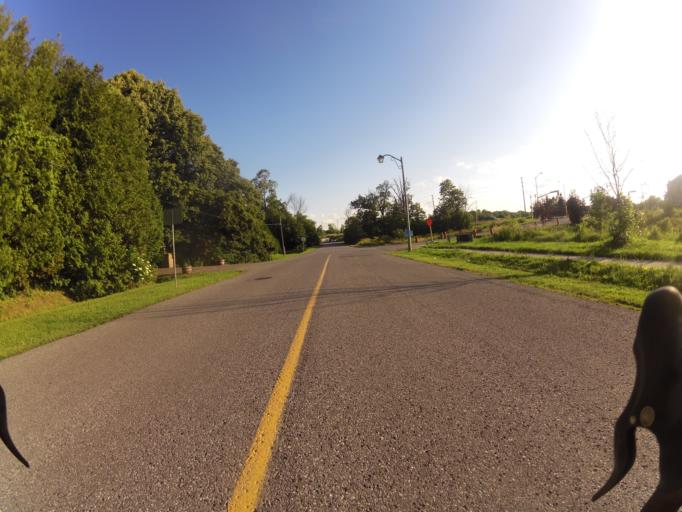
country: CA
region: Ontario
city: Ottawa
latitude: 45.2810
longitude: -75.7021
